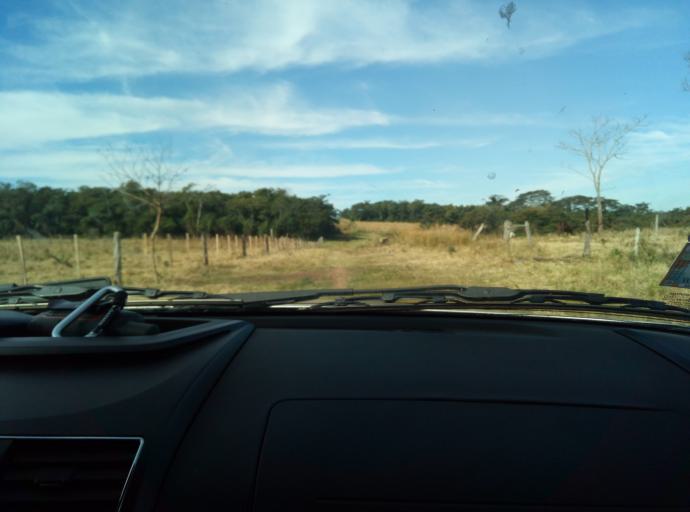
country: PY
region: Caaguazu
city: Carayao
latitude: -25.1725
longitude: -56.2847
